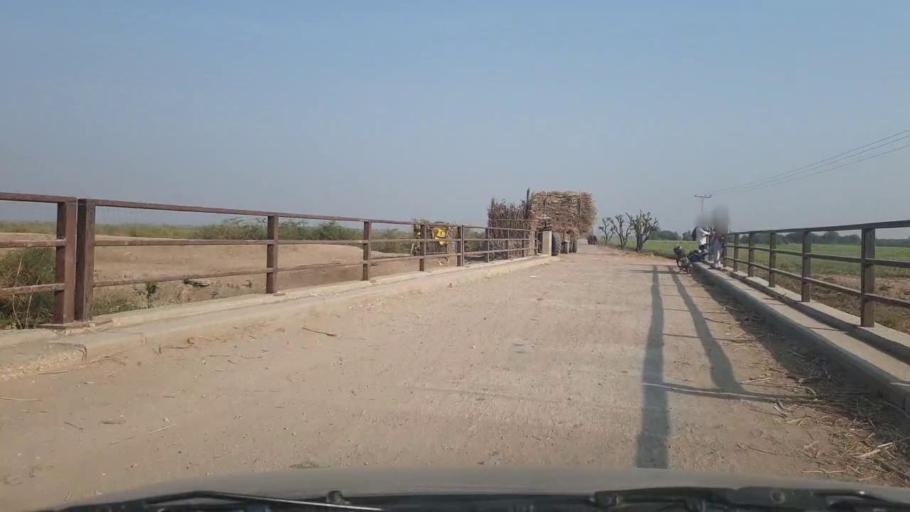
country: PK
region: Sindh
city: Digri
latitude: 25.2402
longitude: 69.1897
